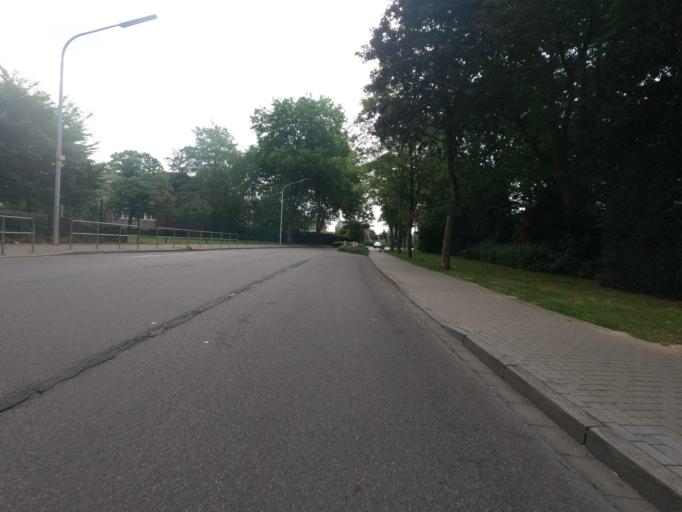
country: DE
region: North Rhine-Westphalia
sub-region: Regierungsbezirk Koln
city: Wassenberg
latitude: 51.0578
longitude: 6.1476
